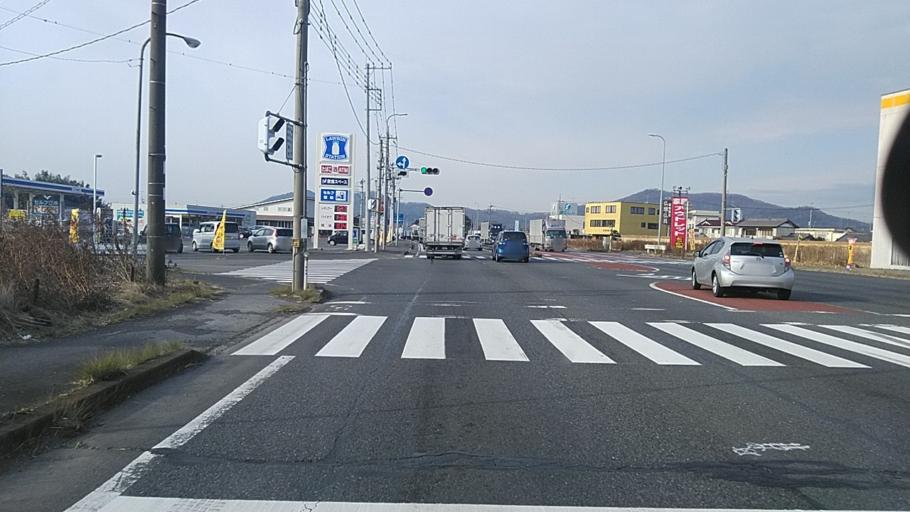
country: JP
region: Tochigi
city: Fujioka
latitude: 36.3143
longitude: 139.6600
